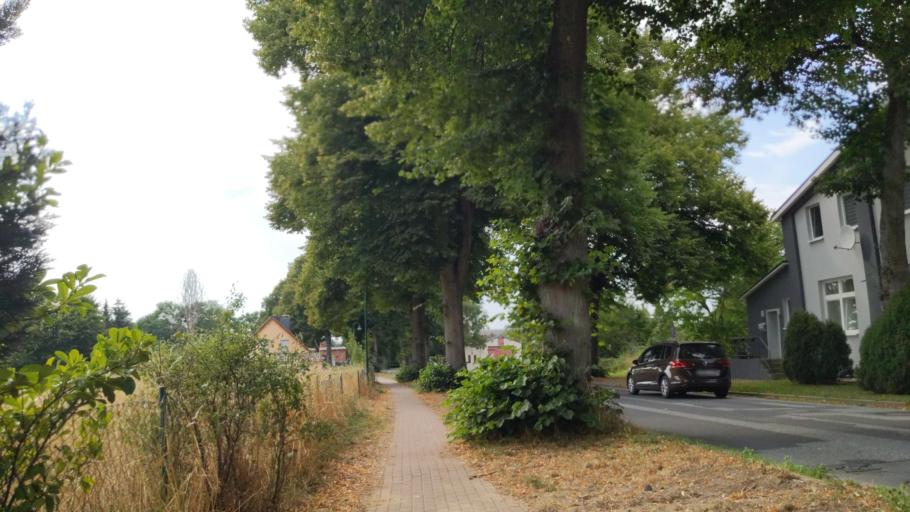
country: DE
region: Schleswig-Holstein
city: Gross Gronau
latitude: 53.8280
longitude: 10.8141
